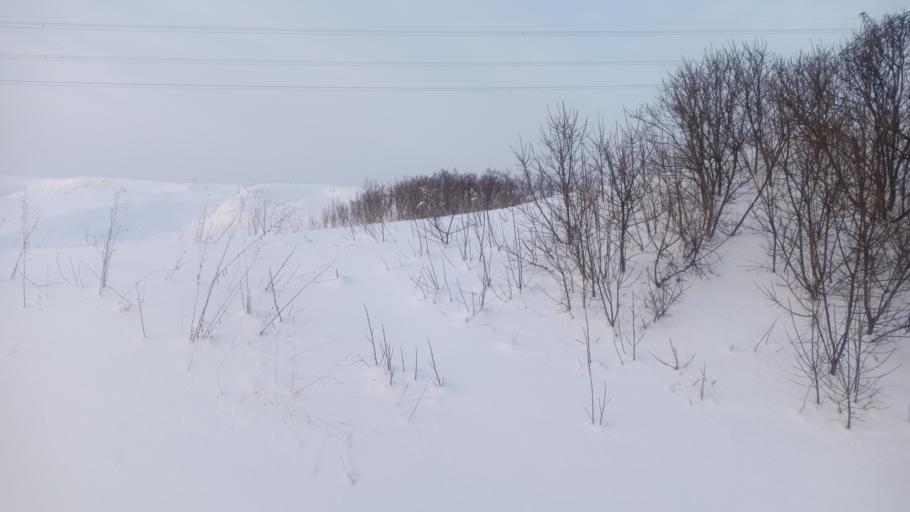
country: RU
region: Altai Krai
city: Nauchnyy Gorodok
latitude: 53.4046
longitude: 83.5139
